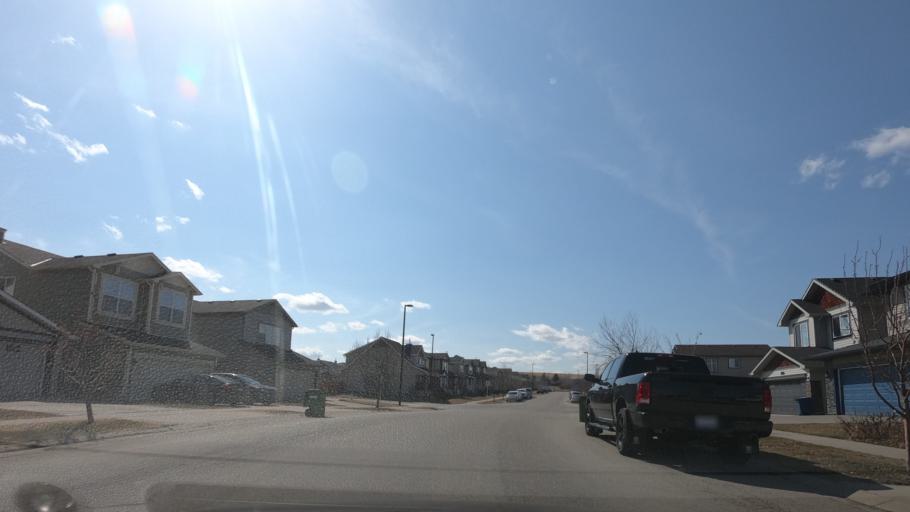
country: CA
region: Alberta
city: Airdrie
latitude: 51.2883
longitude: -114.0442
